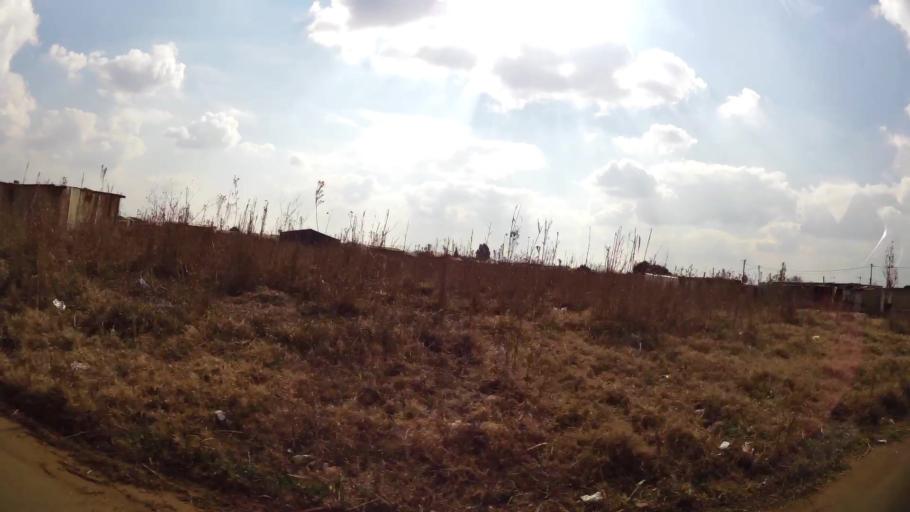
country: ZA
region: Gauteng
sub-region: Ekurhuleni Metropolitan Municipality
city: Springs
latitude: -26.1334
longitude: 28.4757
